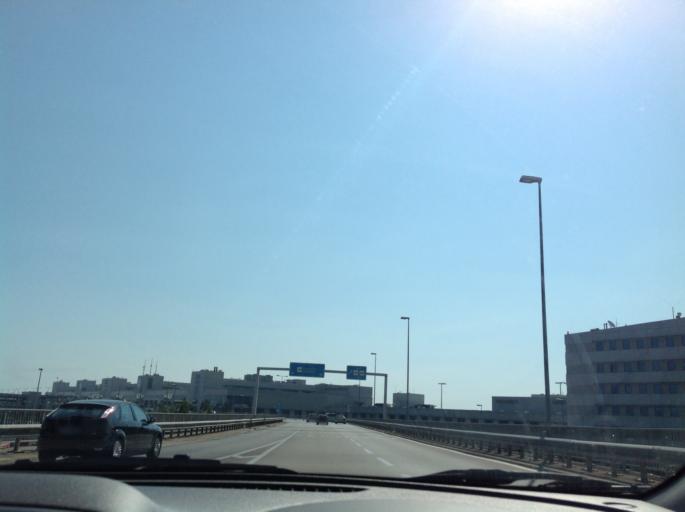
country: GR
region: Attica
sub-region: Nomarchia Anatolikis Attikis
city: Spata
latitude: 37.9342
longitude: 23.9429
